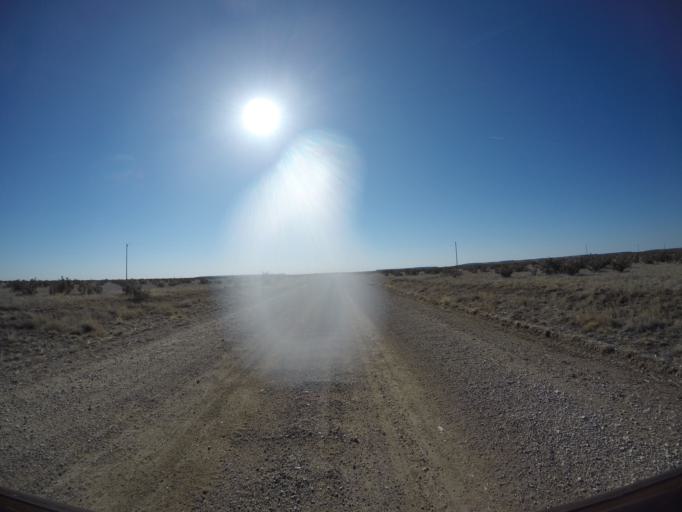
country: US
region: Colorado
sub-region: Otero County
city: La Junta
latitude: 37.6654
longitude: -103.6204
